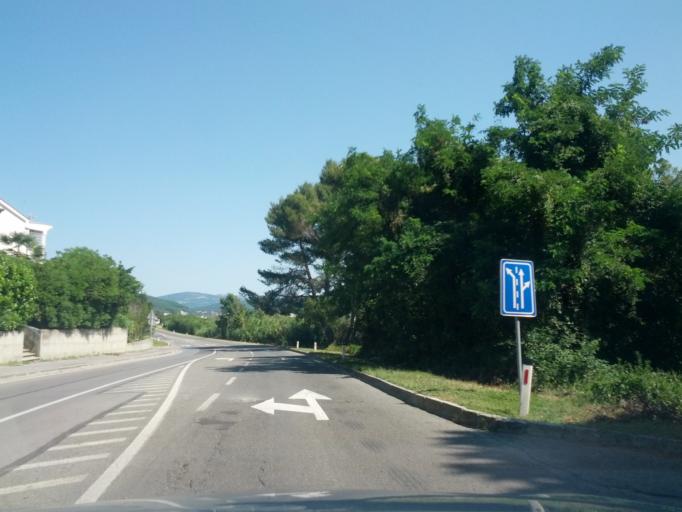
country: SI
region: Koper-Capodistria
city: Hrvatini
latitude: 45.5716
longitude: 13.7493
